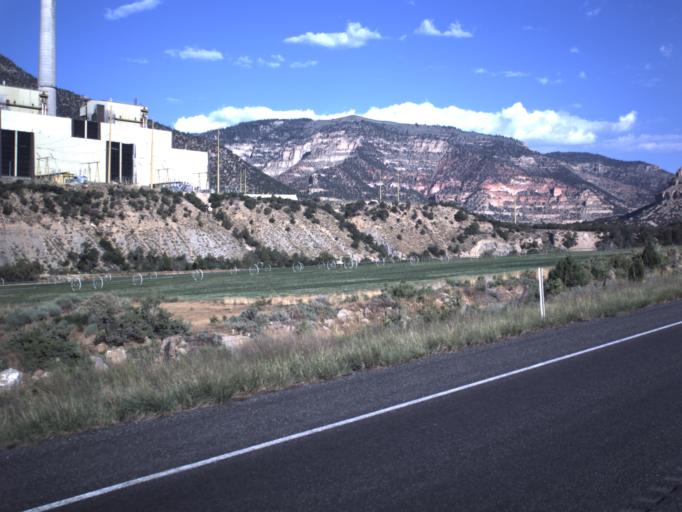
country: US
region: Utah
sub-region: Emery County
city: Huntington
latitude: 39.3794
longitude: -111.0713
